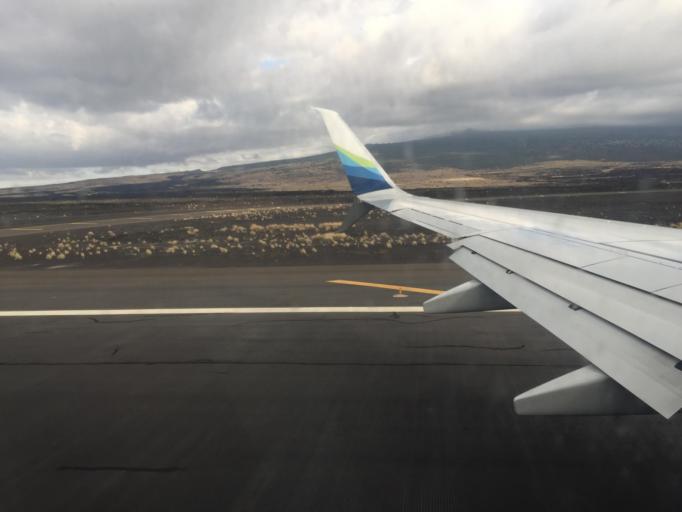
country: US
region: Hawaii
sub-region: Hawaii County
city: Kalaoa
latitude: 19.7528
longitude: -156.0444
